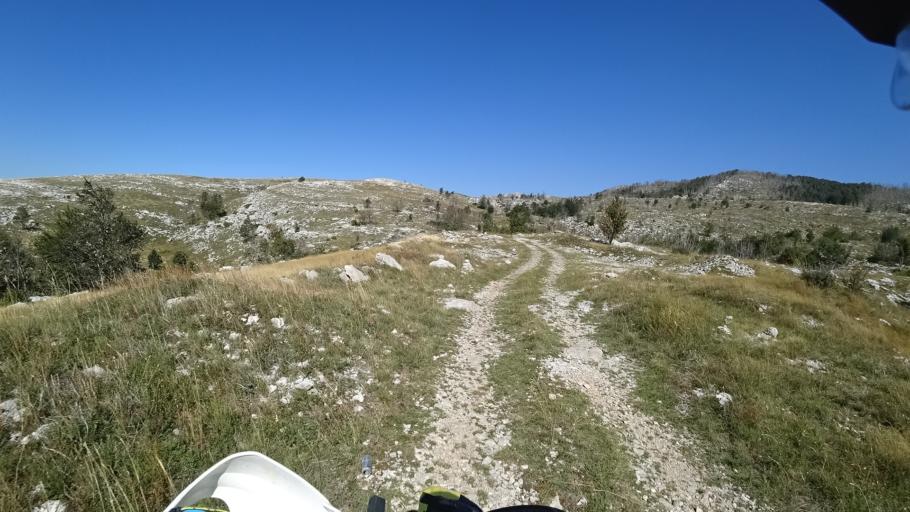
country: HR
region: Splitsko-Dalmatinska
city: Hrvace
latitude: 43.9101
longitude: 16.6122
